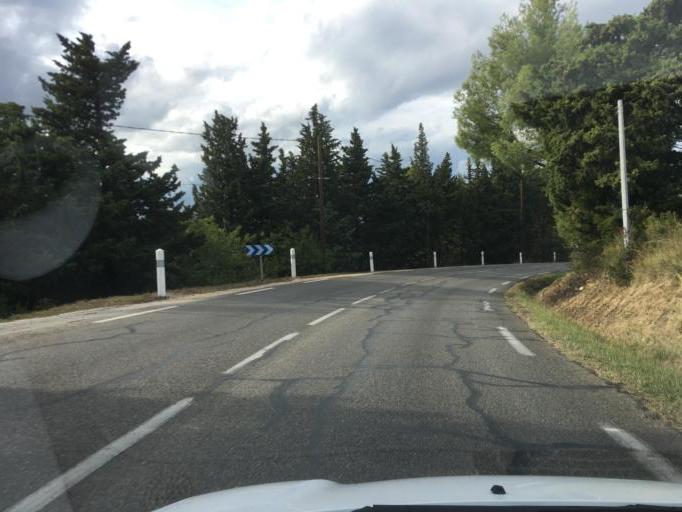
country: FR
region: Provence-Alpes-Cote d'Azur
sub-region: Departement du Vaucluse
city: Jonquerettes
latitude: 43.9318
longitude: 4.9230
